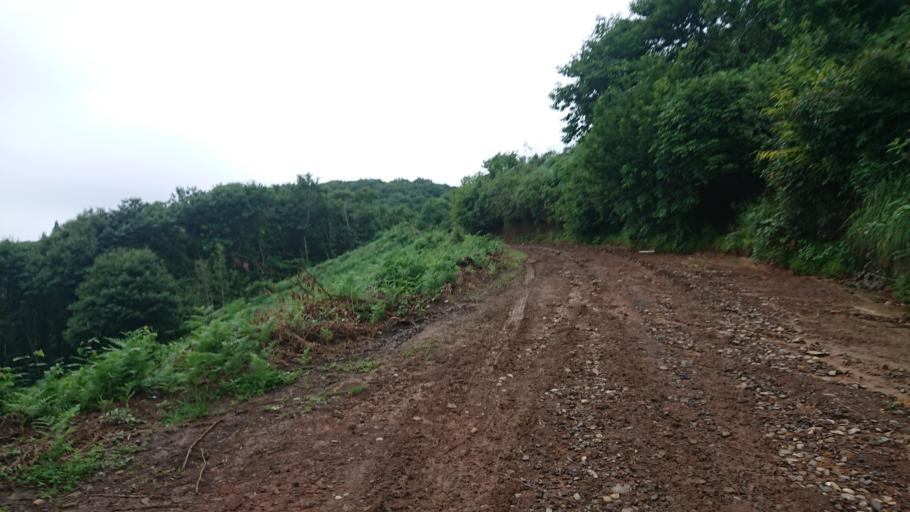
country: TR
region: Rize
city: Rize
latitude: 40.9886
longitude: 40.5070
